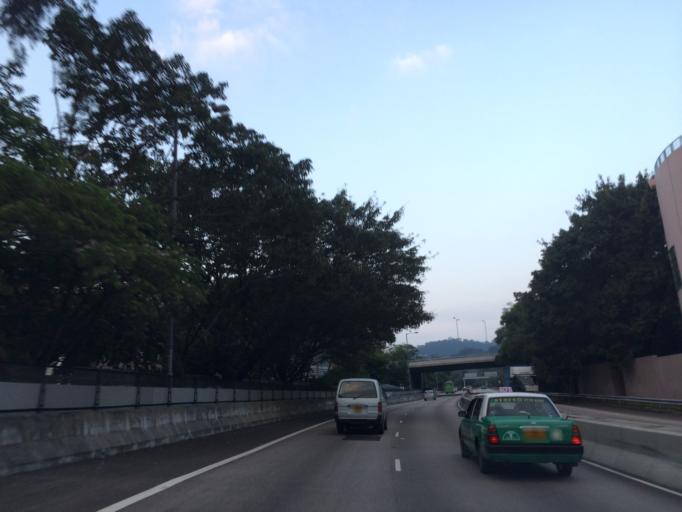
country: HK
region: Sha Tin
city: Sha Tin
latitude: 22.3921
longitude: 114.1983
